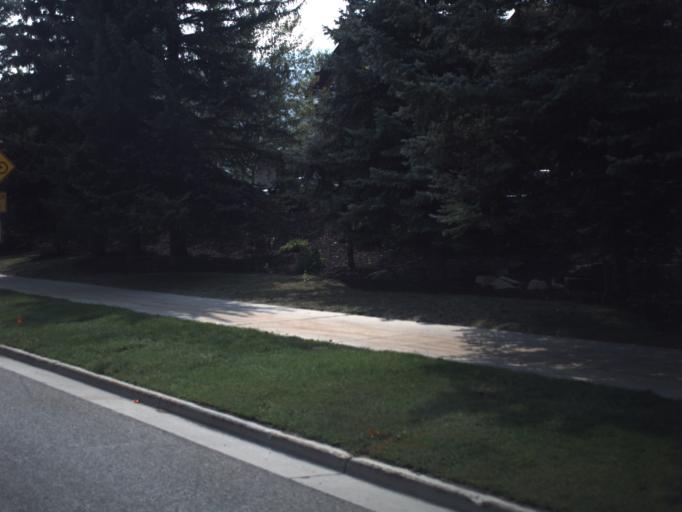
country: US
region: Utah
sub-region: Summit County
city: Park City
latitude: 40.6623
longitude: -111.5125
